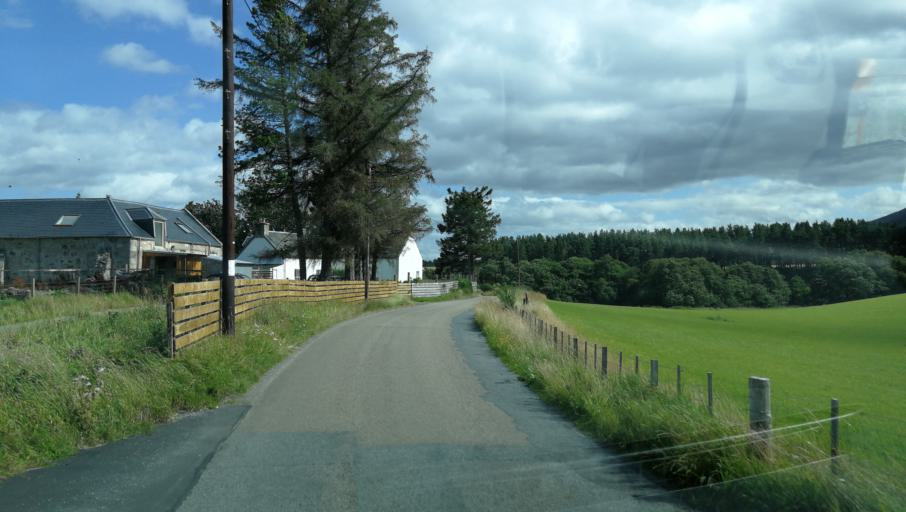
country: GB
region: Scotland
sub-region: Highland
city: Aviemore
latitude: 57.2175
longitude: -3.7646
